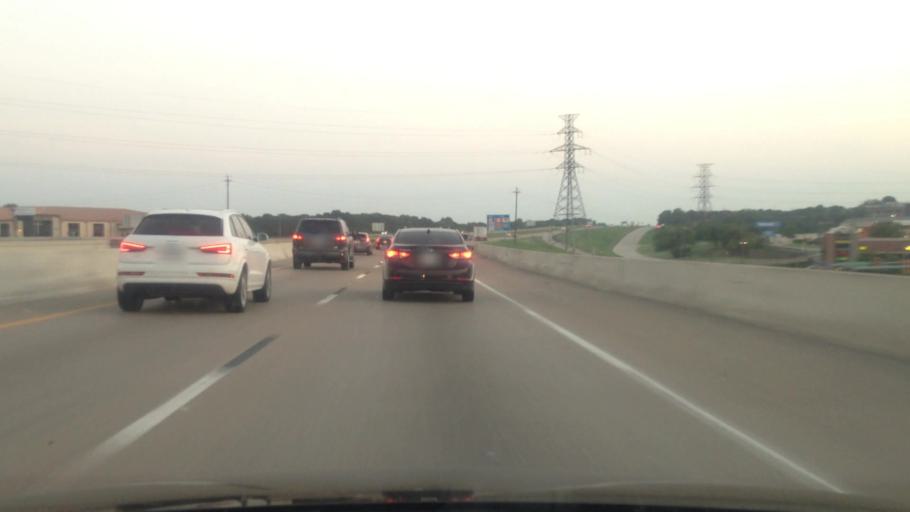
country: US
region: Texas
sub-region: Tarrant County
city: Euless
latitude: 32.8665
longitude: -97.1017
